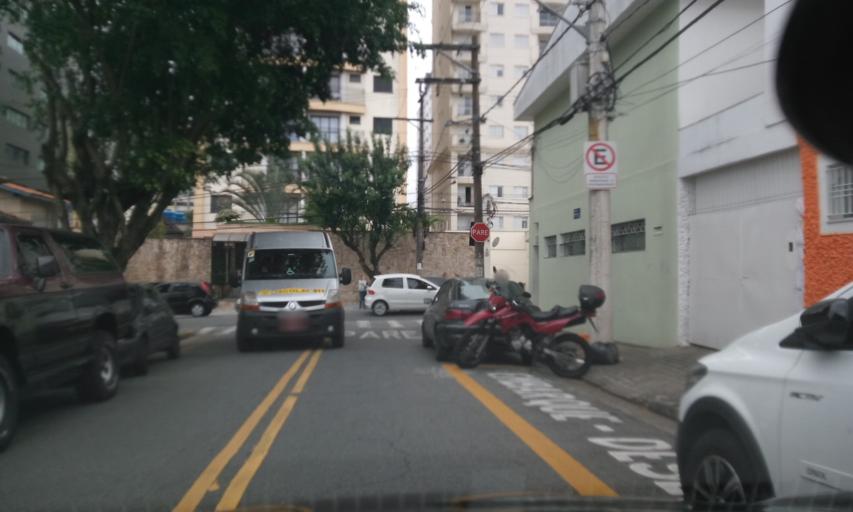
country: BR
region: Sao Paulo
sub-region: Sao Caetano Do Sul
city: Sao Caetano do Sul
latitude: -23.6223
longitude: -46.5726
